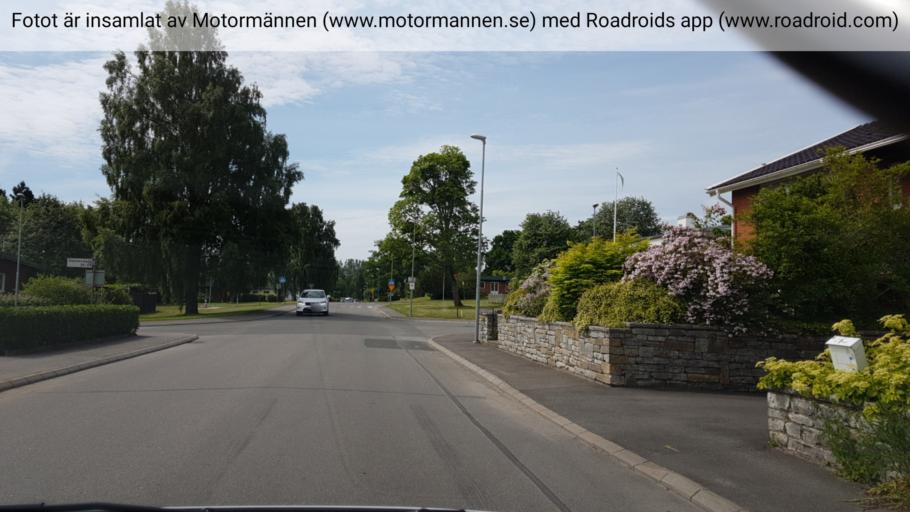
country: SE
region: Vaestra Goetaland
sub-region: Skovde Kommun
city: Skoevde
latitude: 58.3959
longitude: 13.8228
